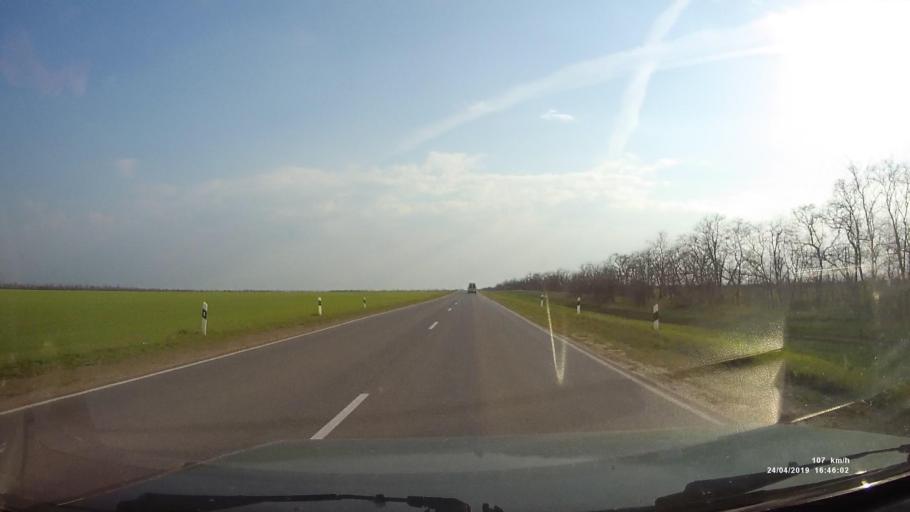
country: RU
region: Rostov
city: Gundorovskiy
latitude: 46.7622
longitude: 41.8065
